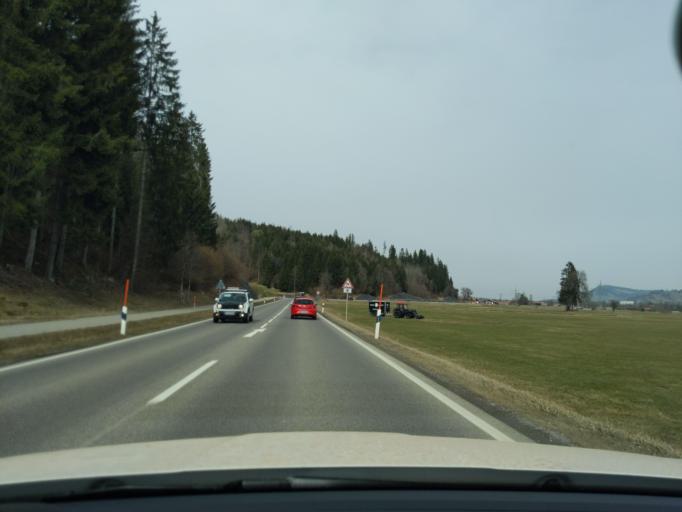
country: DE
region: Bavaria
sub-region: Swabia
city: Sonthofen
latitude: 47.4940
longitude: 10.2665
